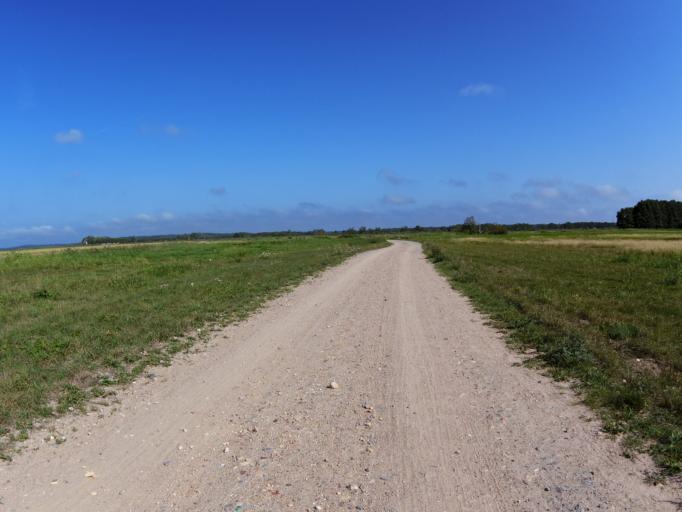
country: DE
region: Mecklenburg-Vorpommern
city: Loddin
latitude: 53.9731
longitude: 14.0509
